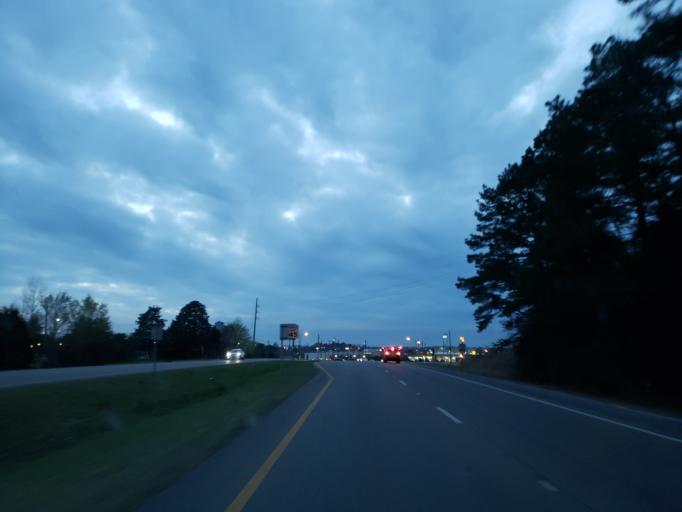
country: US
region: Mississippi
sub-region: Lauderdale County
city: Meridian
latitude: 32.3639
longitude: -88.6642
